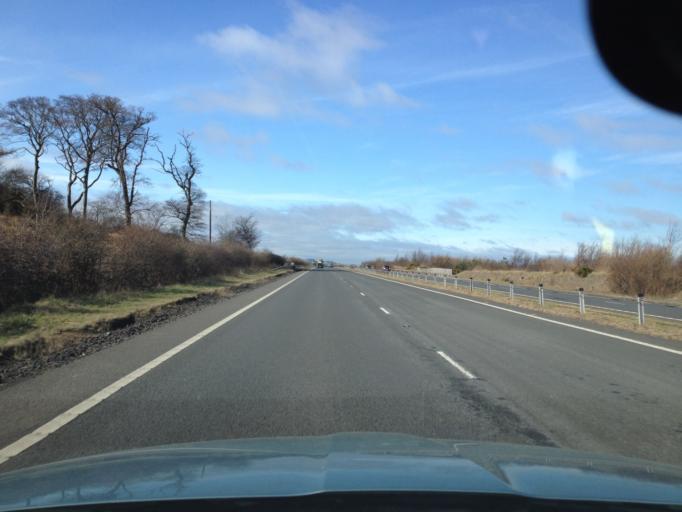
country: GB
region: Scotland
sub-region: East Lothian
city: East Linton
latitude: 55.9879
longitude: -2.6151
